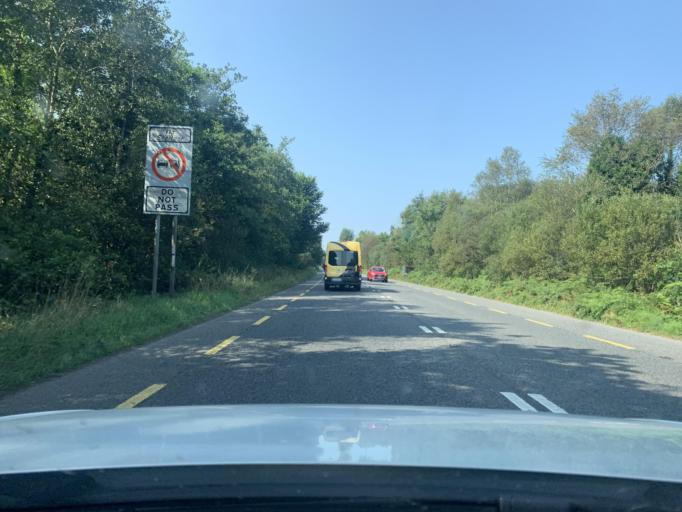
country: IE
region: Leinster
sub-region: An Iarmhi
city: Athlone
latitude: 53.4521
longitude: -7.9893
